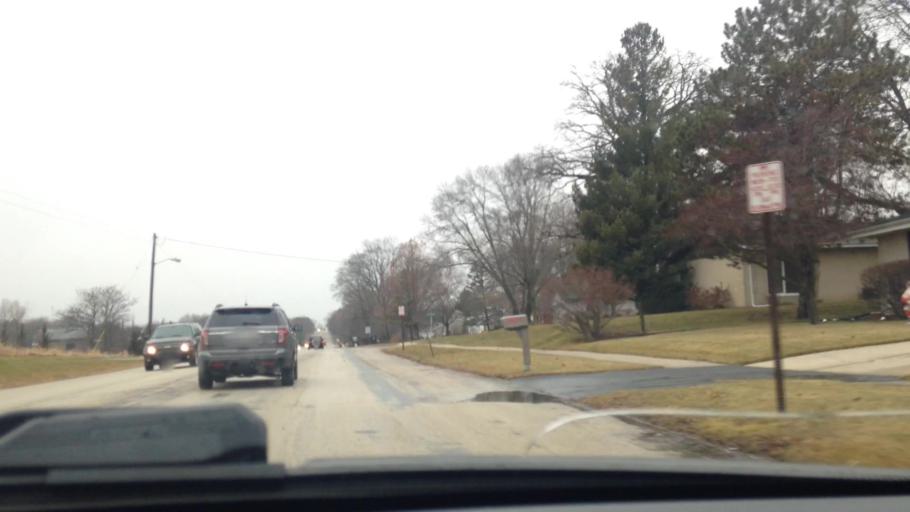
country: US
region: Wisconsin
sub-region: Waukesha County
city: Menomonee Falls
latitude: 43.1703
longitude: -88.1275
